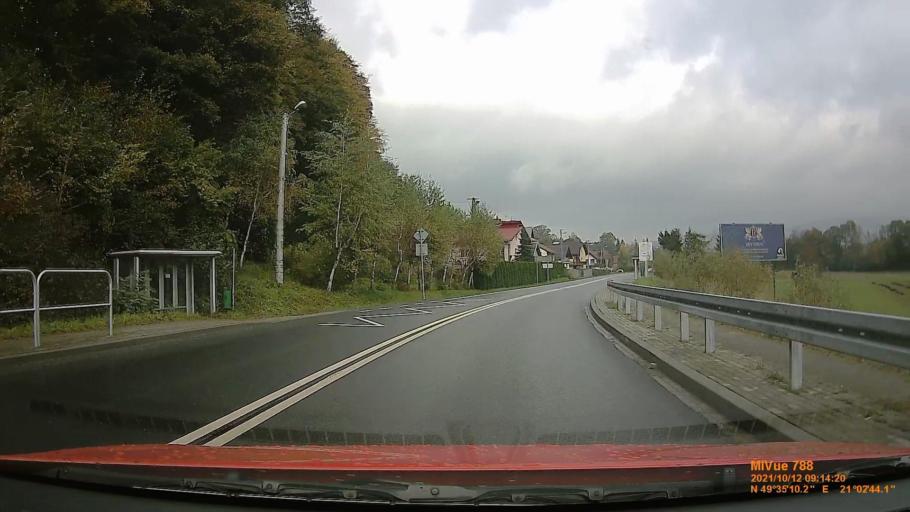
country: PL
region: Lesser Poland Voivodeship
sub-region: Powiat gorlicki
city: Ropa
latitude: 49.5863
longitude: 21.0454
